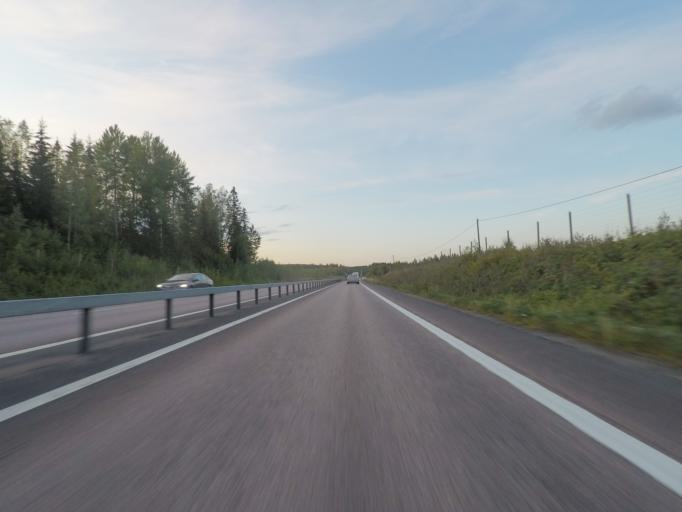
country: FI
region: Central Finland
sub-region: Jyvaeskylae
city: Saeynaetsalo
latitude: 62.2173
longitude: 25.8927
